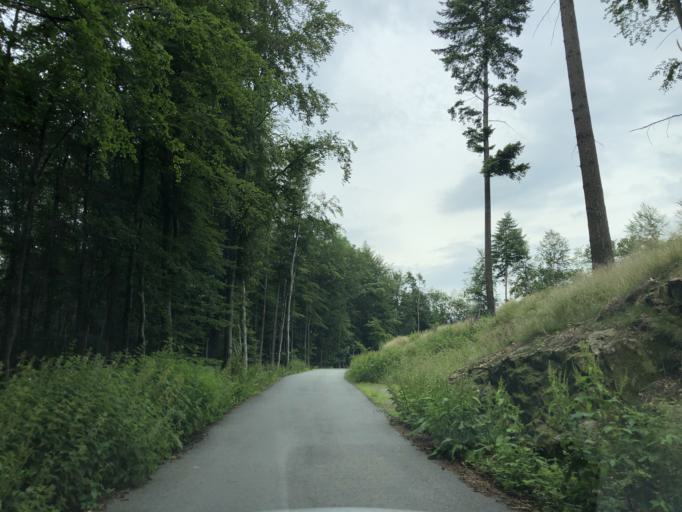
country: DE
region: Hesse
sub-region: Regierungsbezirk Darmstadt
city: Seeheim-Jugenheim
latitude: 49.7303
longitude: 8.6817
